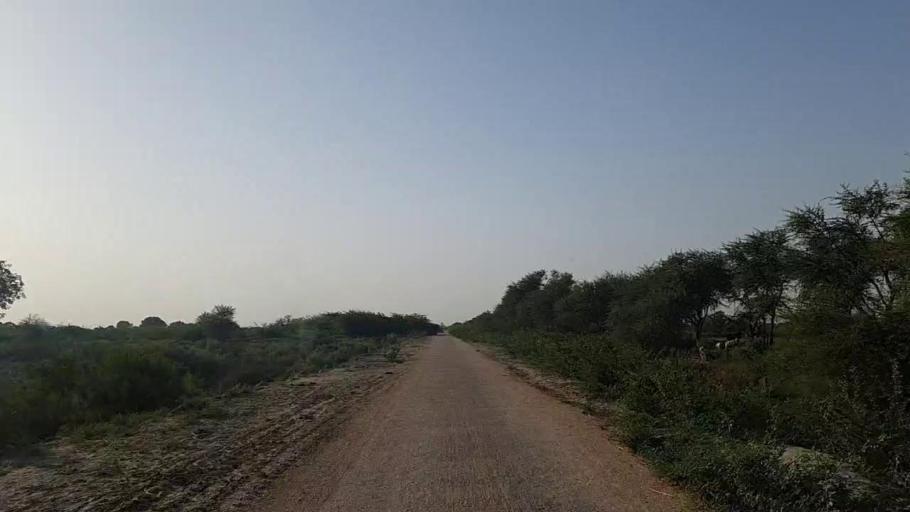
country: PK
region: Sindh
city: Jati
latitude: 24.3356
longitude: 68.1536
